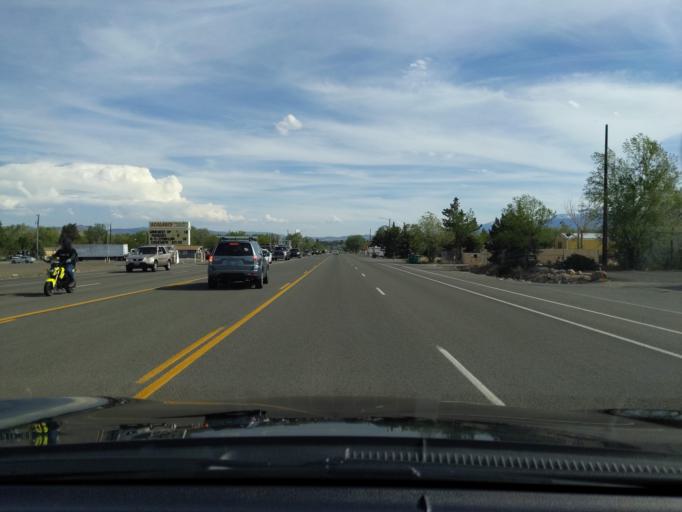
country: US
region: Nevada
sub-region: Washoe County
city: Sun Valley
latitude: 39.5914
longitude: -119.7806
